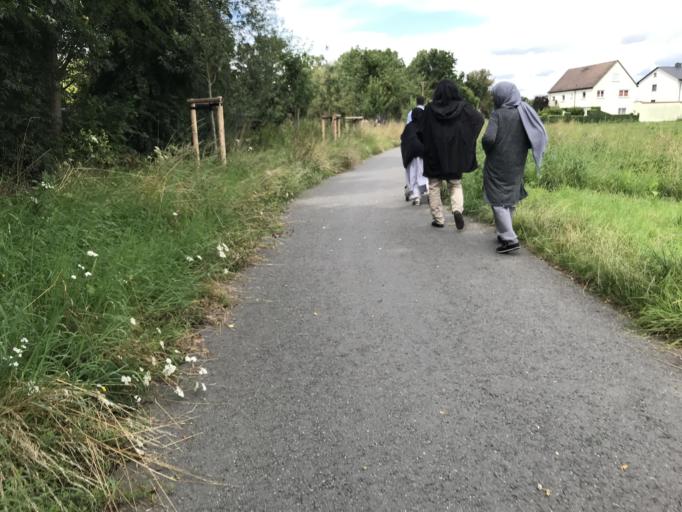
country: DE
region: Hesse
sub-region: Regierungsbezirk Darmstadt
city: Friedberg
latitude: 50.3308
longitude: 8.7750
